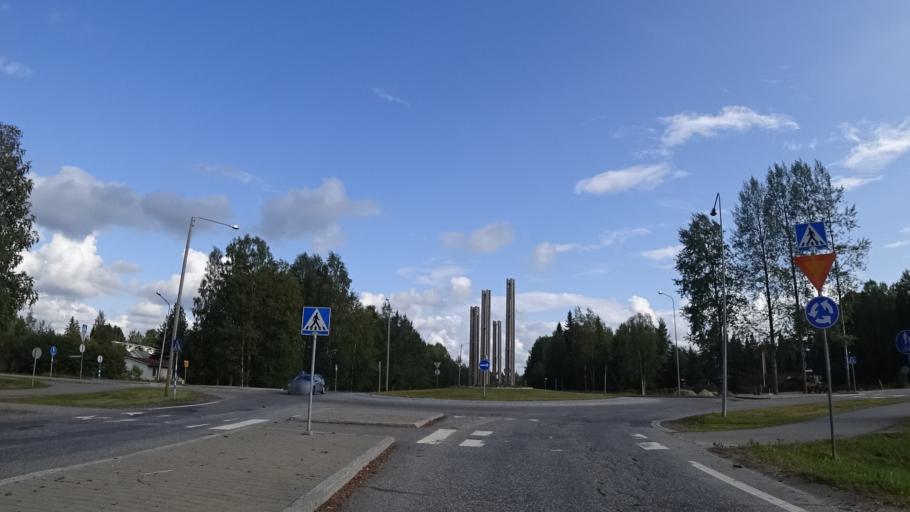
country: FI
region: North Karelia
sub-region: Pielisen Karjala
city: Lieksa
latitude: 63.3228
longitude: 30.0092
